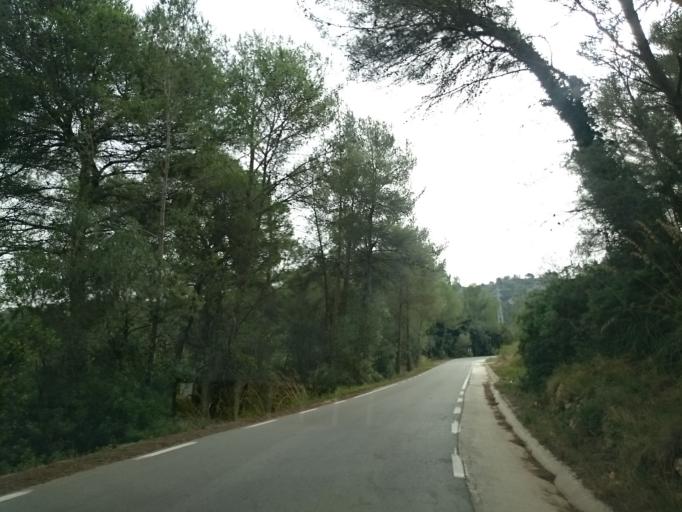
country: ES
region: Catalonia
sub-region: Provincia de Barcelona
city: Olivella
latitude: 41.3126
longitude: 1.8042
